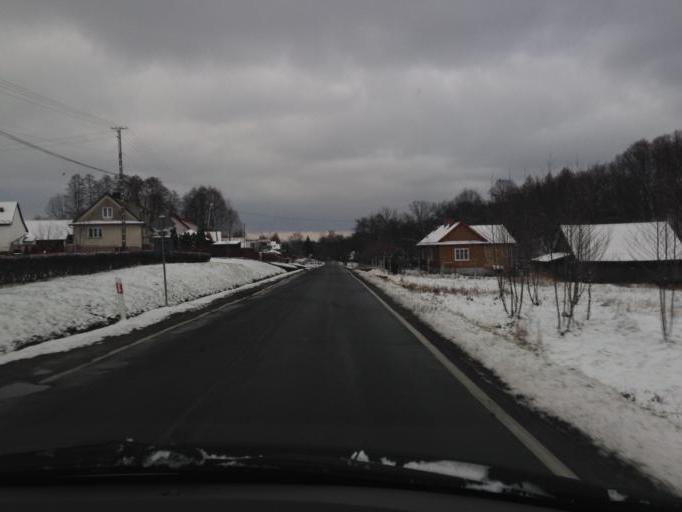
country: PL
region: Lesser Poland Voivodeship
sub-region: Powiat brzeski
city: Iwkowa
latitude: 49.8510
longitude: 20.5986
